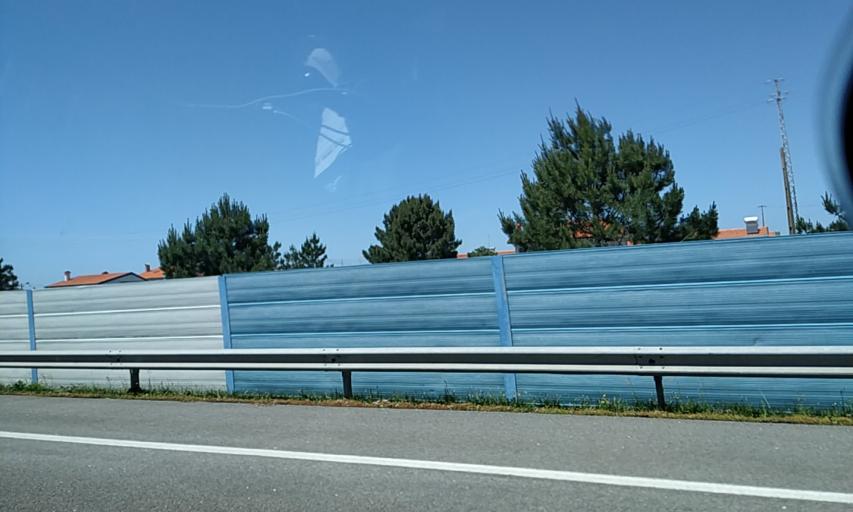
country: PT
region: Aveiro
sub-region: Ilhavo
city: Gafanha da Nazare
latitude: 40.6296
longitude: -8.6985
